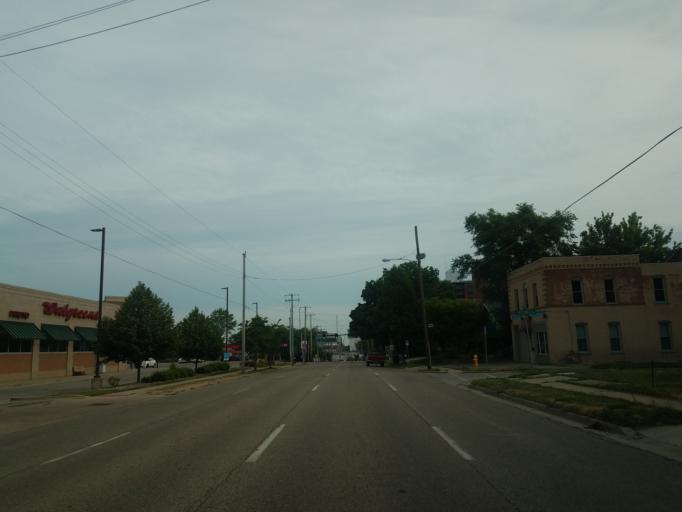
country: US
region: Illinois
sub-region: McLean County
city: Bloomington
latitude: 40.4703
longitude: -88.9932
